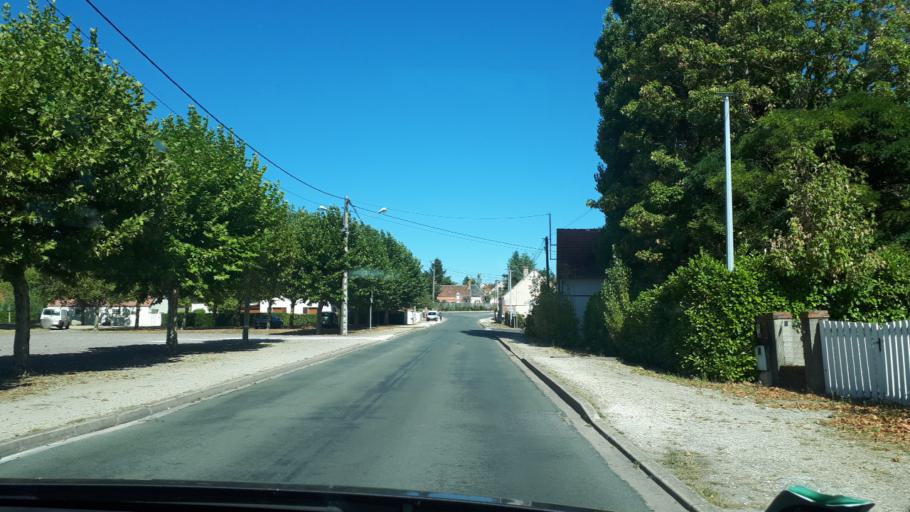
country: FR
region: Centre
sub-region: Departement du Loiret
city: Coullons
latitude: 47.6240
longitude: 2.4913
